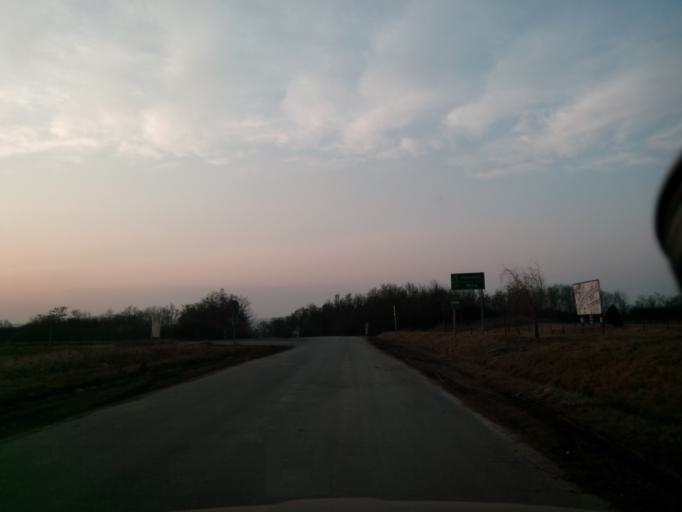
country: HU
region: Borsod-Abauj-Zemplen
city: Gonc
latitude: 48.4781
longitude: 21.2620
